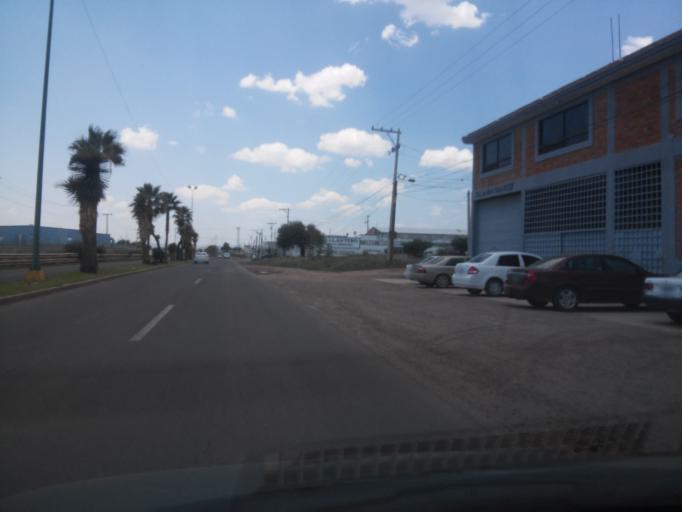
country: MX
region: Durango
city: Victoria de Durango
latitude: 24.0716
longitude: -104.6091
